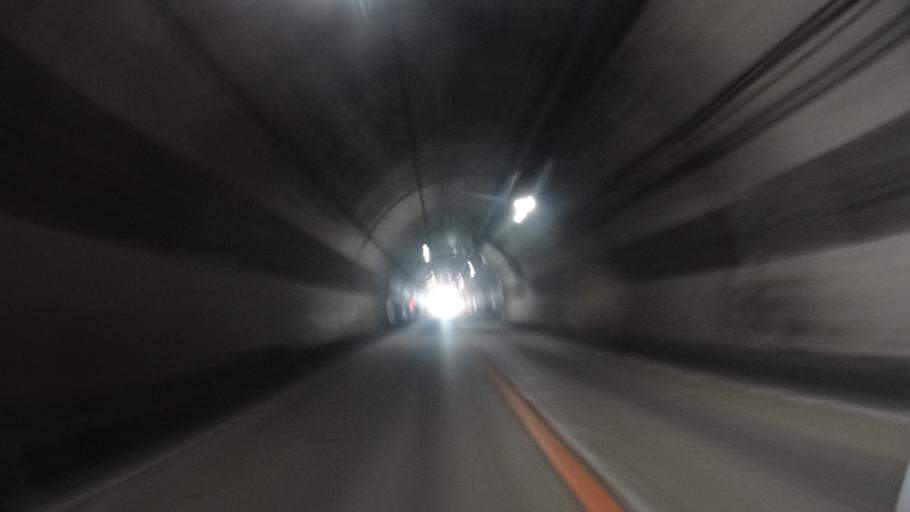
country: JP
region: Shimane
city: Masuda
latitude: 34.6649
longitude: 131.6870
